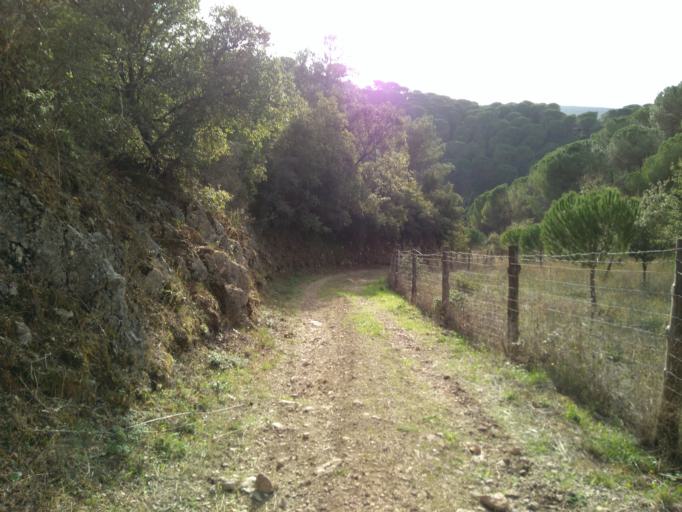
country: PT
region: Leiria
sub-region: Porto de Mos
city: Porto de Mos
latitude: 39.5921
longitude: -8.8066
